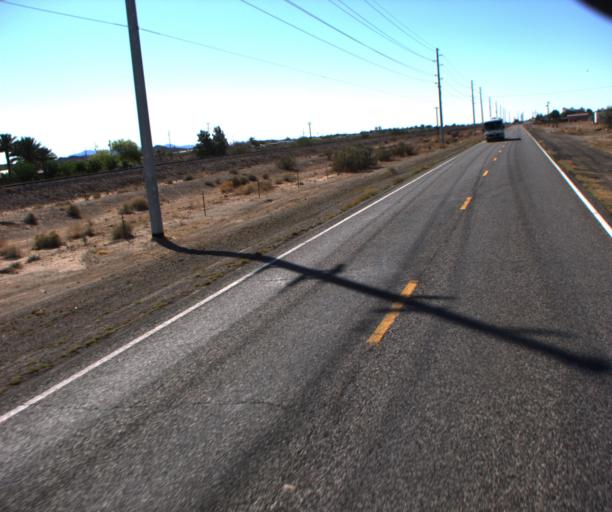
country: US
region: Arizona
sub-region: La Paz County
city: Cienega Springs
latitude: 33.9435
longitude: -114.0141
